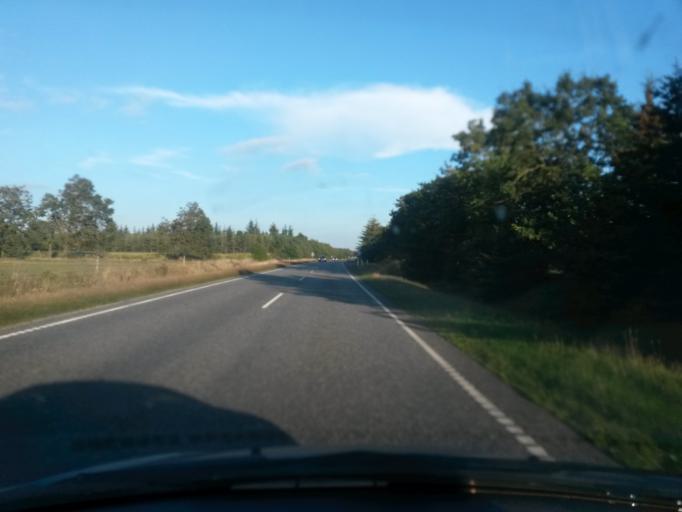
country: DK
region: Central Jutland
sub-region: Herning Kommune
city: Sunds
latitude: 56.3319
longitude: 8.9713
